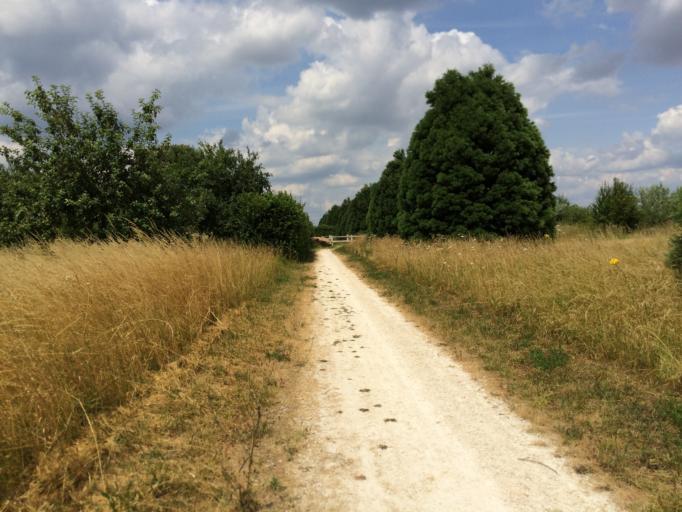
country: FR
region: Ile-de-France
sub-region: Departement de Seine-et-Marne
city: Lieusaint
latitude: 48.6287
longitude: 2.5282
